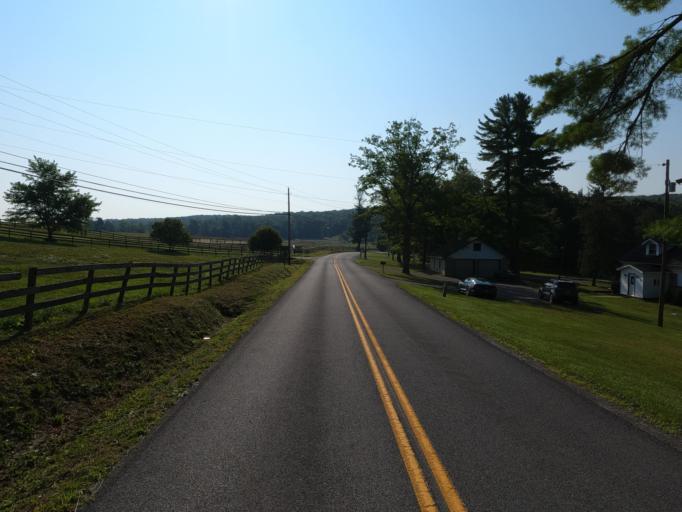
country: US
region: Maryland
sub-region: Garrett County
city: Mountain Lake Park
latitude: 39.4960
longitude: -79.3484
